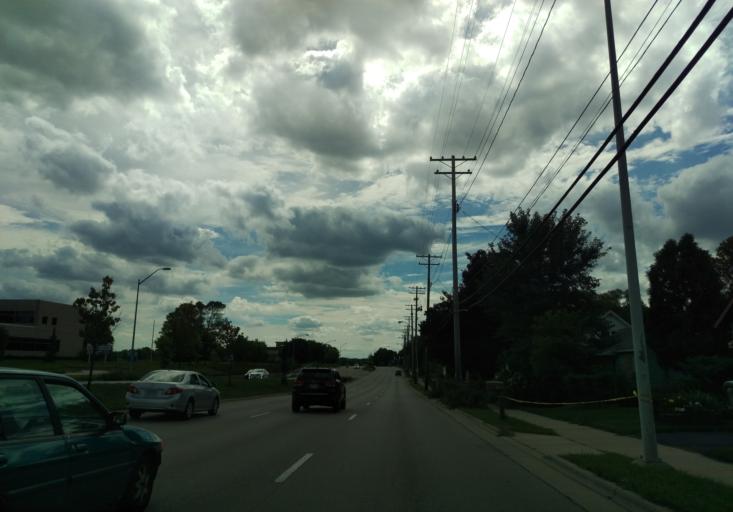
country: US
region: Wisconsin
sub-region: Dane County
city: Maple Bluff
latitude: 43.1200
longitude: -89.3551
